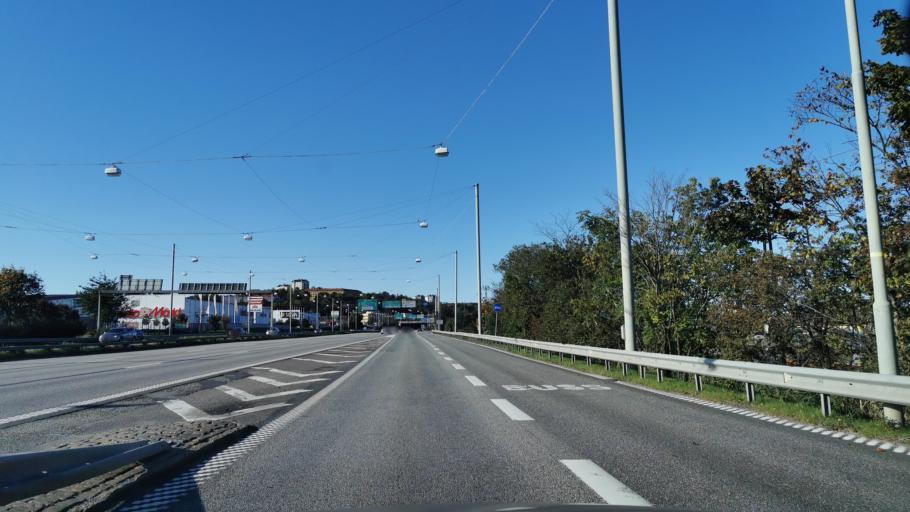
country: SE
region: Vaestra Goetaland
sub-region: Goteborg
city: Eriksbo
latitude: 57.7263
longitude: 12.0344
